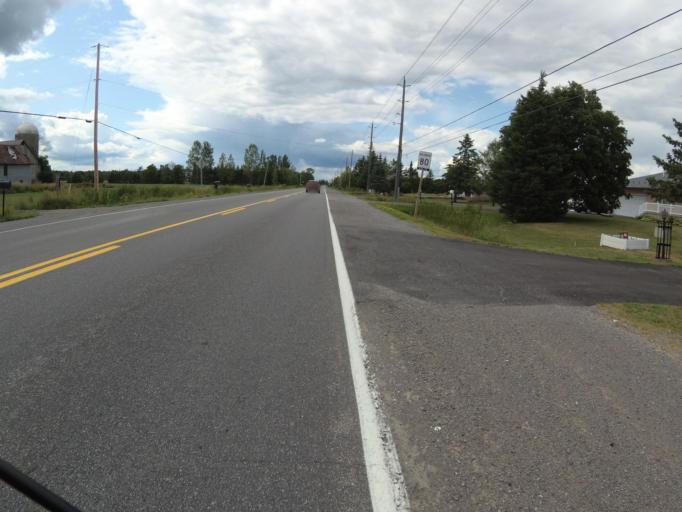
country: CA
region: Ontario
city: Bells Corners
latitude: 45.4461
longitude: -76.0411
